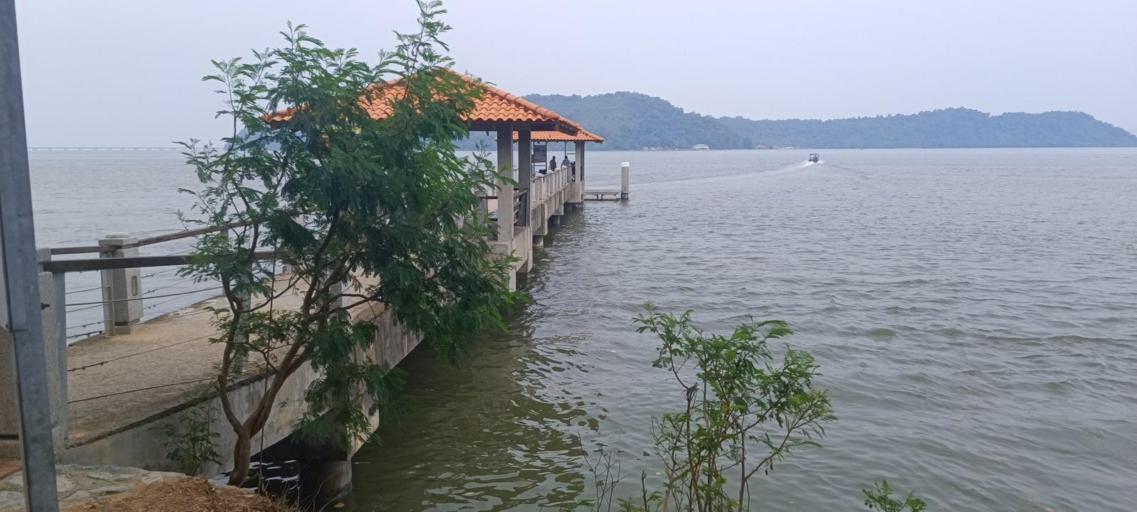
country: MY
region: Penang
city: Juru
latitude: 5.2657
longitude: 100.4061
